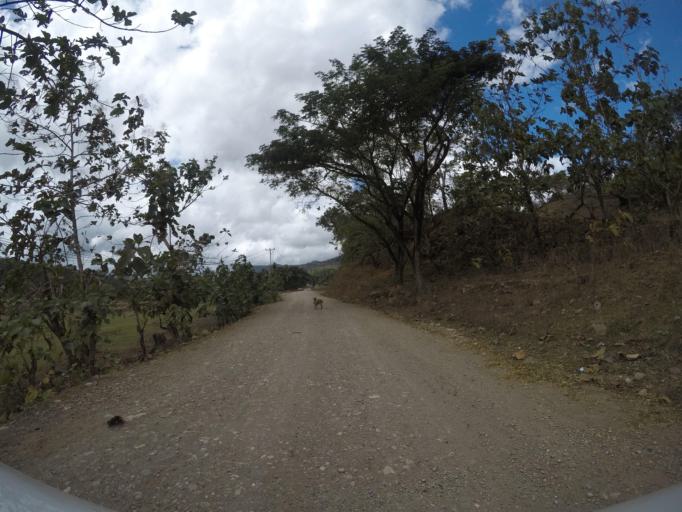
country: TL
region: Lautem
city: Lospalos
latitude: -8.5063
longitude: 126.8319
